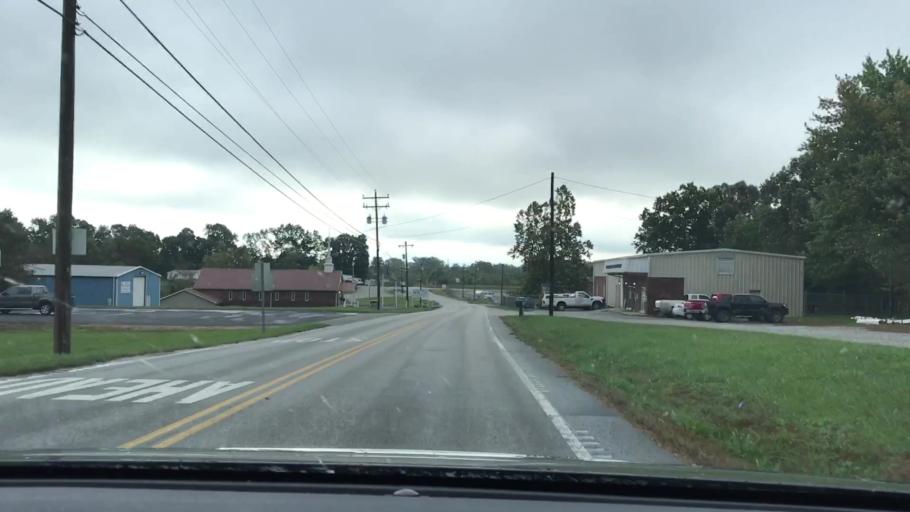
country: US
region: Tennessee
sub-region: Fentress County
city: Jamestown
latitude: 36.3882
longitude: -84.9362
